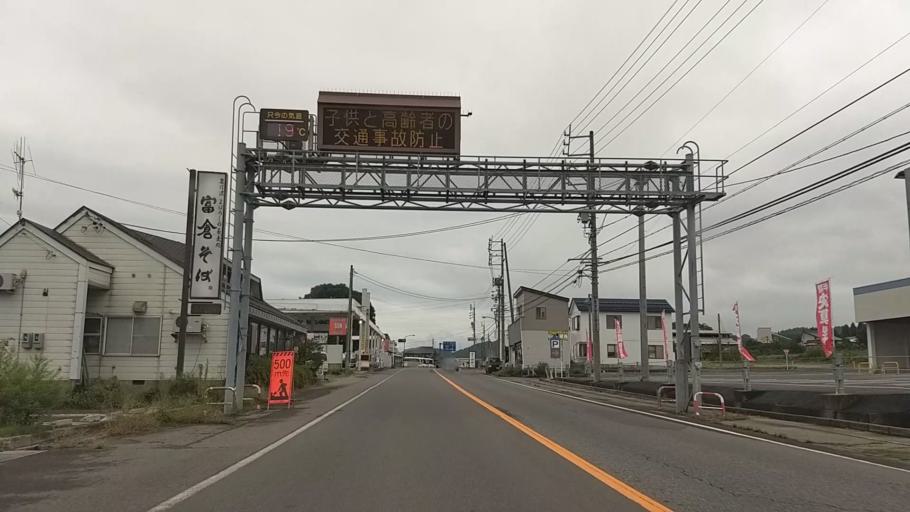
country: JP
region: Nagano
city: Iiyama
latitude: 36.8288
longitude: 138.3543
